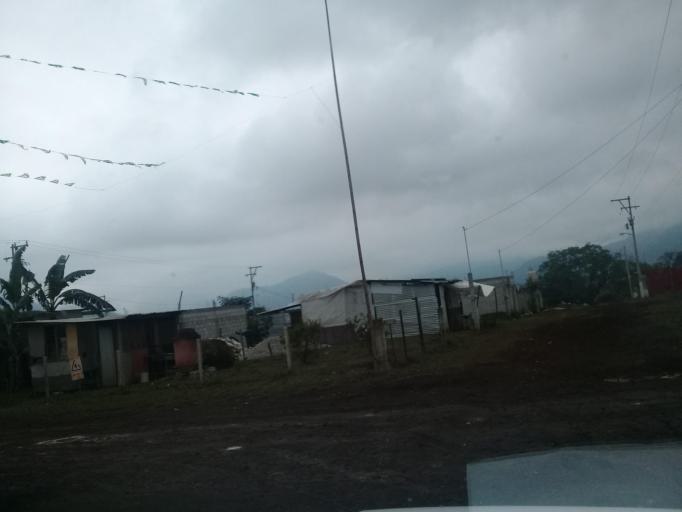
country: MX
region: Veracruz
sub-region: Cordoba
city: San Jose de Tapia
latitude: 18.8530
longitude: -96.9587
